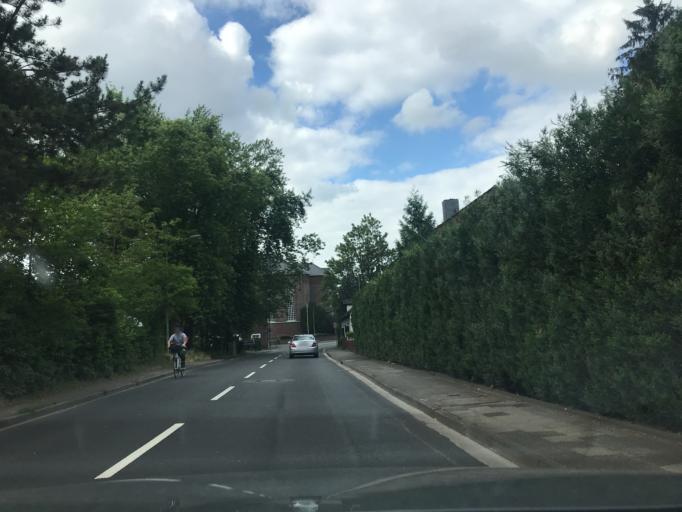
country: DE
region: North Rhine-Westphalia
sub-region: Regierungsbezirk Dusseldorf
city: Neuss
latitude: 51.1318
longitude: 6.7278
